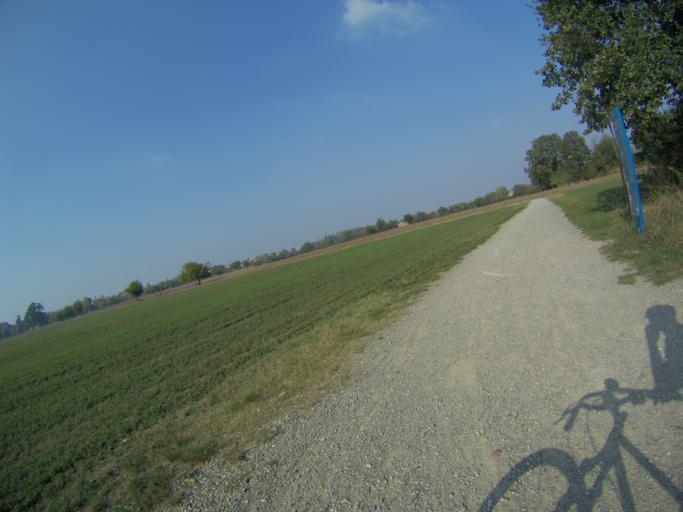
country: IT
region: Emilia-Romagna
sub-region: Provincia di Reggio Emilia
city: Albinea
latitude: 44.6586
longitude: 10.5981
